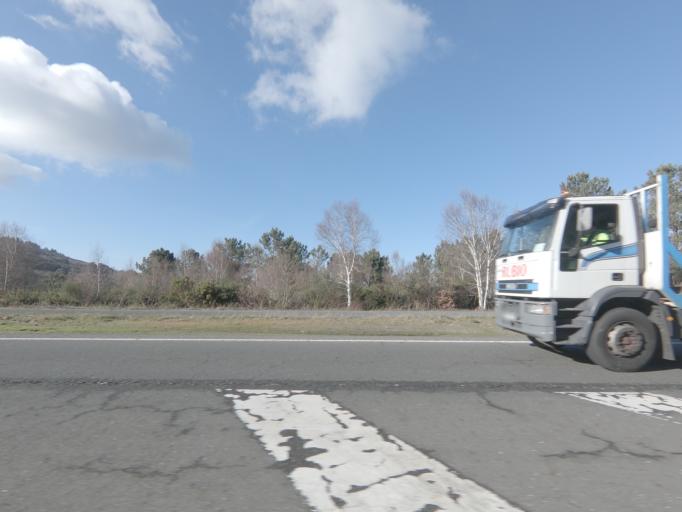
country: ES
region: Galicia
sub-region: Provincia de Pontevedra
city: Silleda
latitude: 42.6985
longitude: -8.3347
